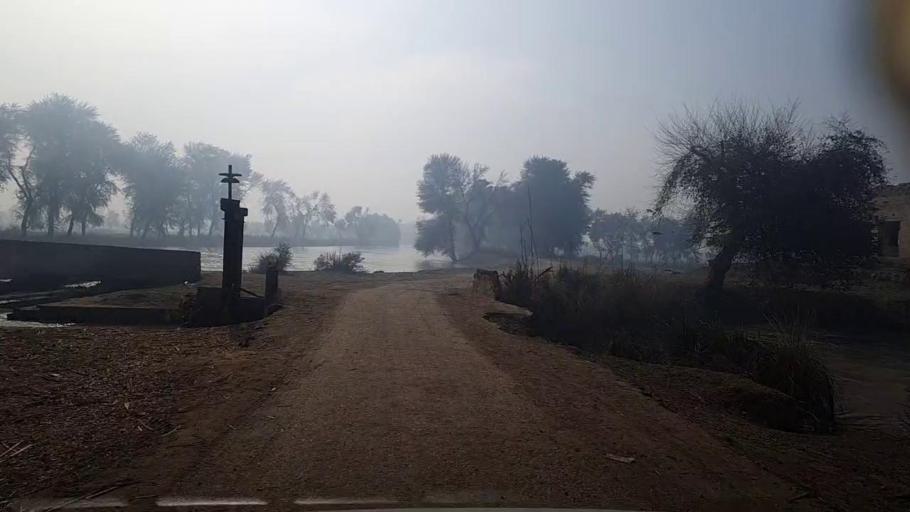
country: PK
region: Sindh
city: Khairpur
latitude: 27.9513
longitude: 69.6523
